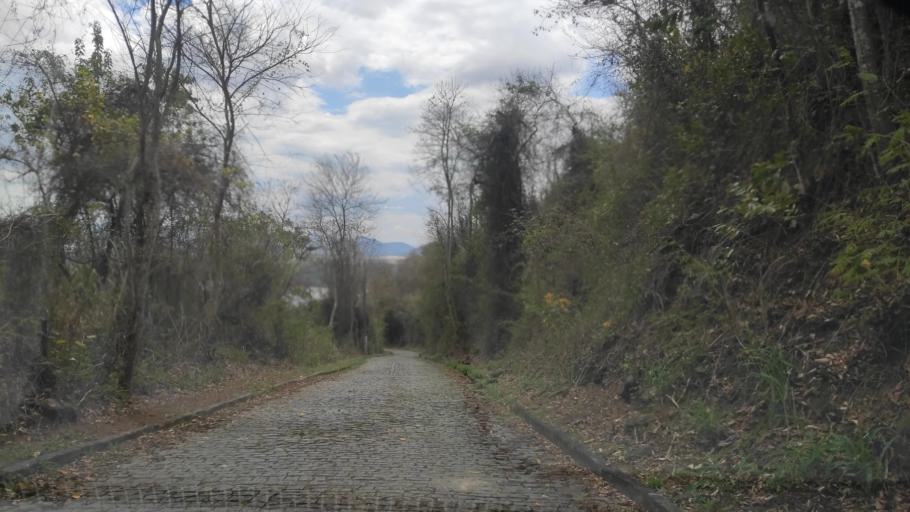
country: BR
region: Espirito Santo
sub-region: Vitoria
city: Vitoria
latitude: -20.2963
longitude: -40.3363
